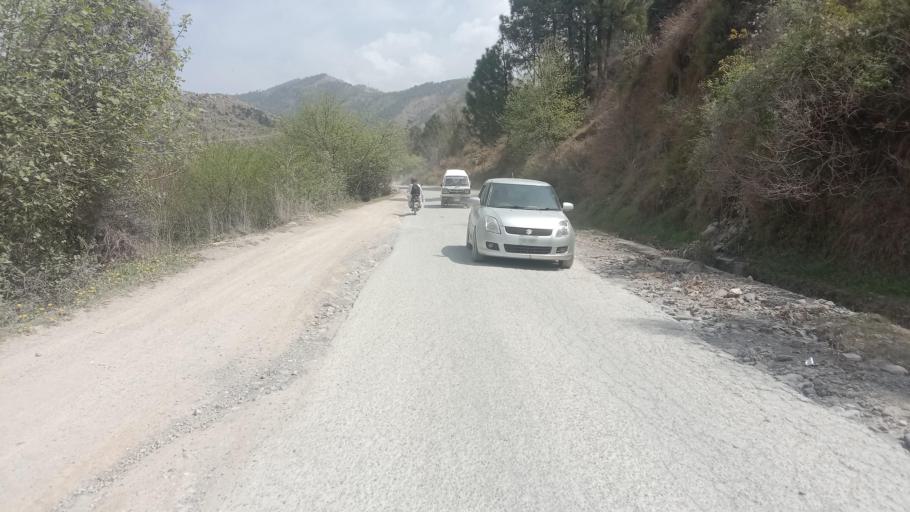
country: PK
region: Khyber Pakhtunkhwa
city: Abbottabad
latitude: 34.1614
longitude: 73.2714
